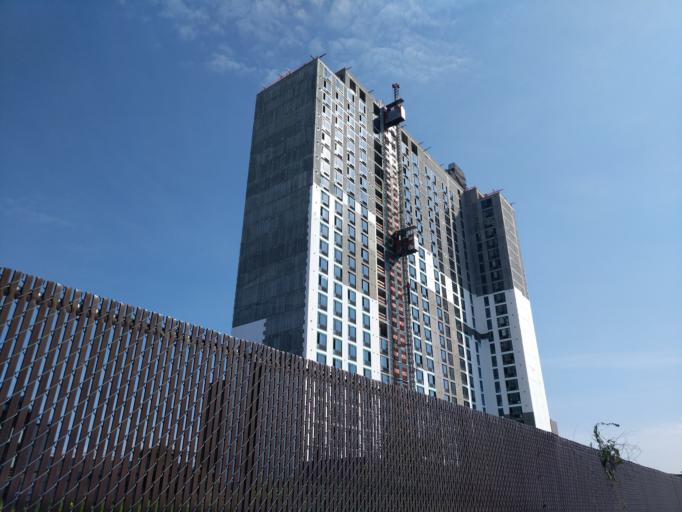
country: US
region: New York
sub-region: Queens County
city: Jamaica
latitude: 40.6985
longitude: -73.8063
